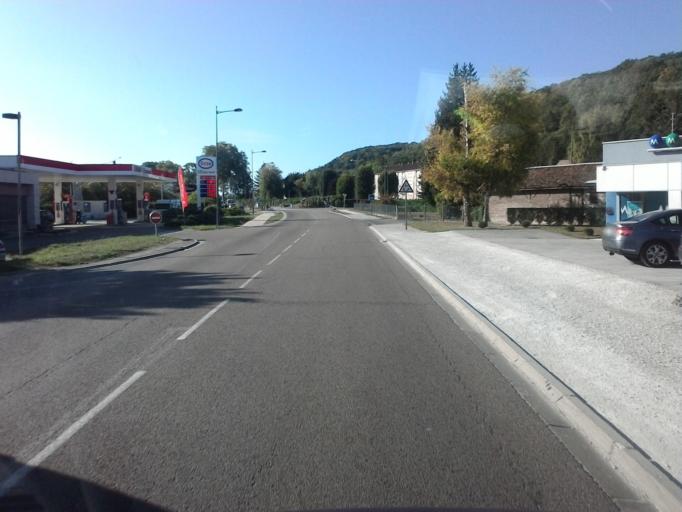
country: FR
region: Champagne-Ardenne
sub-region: Departement de l'Aube
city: Bar-sur-Seine
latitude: 48.1068
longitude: 4.3767
